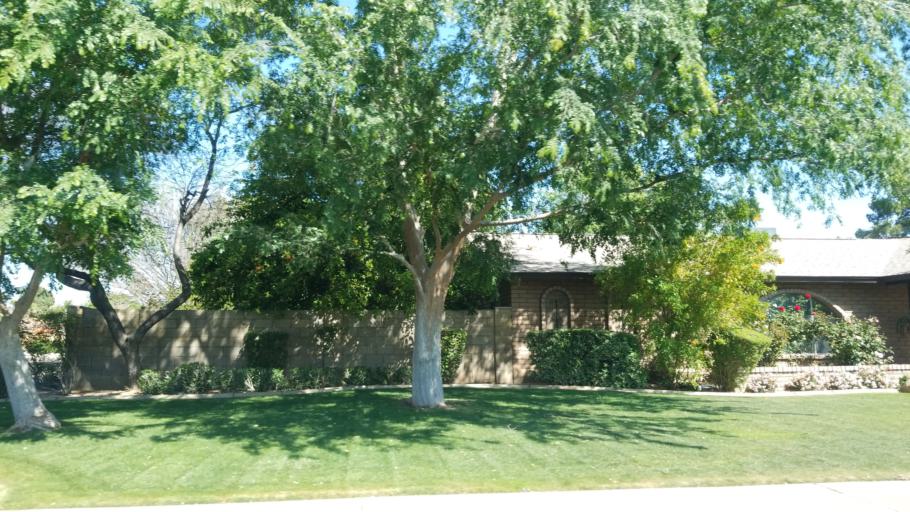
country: US
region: Arizona
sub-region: Maricopa County
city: Glendale
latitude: 33.5602
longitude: -112.1732
